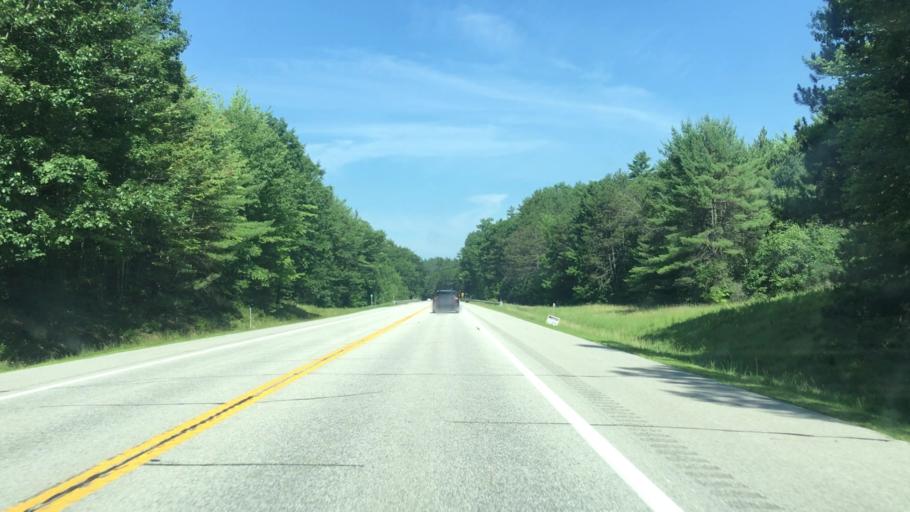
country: US
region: New Hampshire
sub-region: Merrimack County
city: Henniker
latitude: 43.1875
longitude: -71.8063
